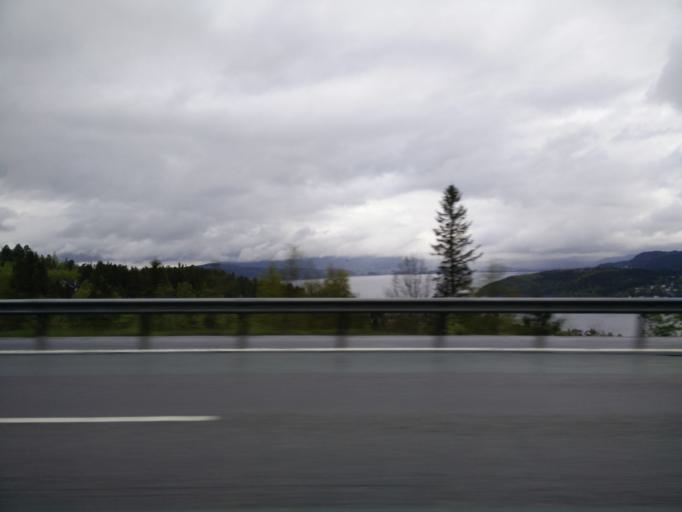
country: NO
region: Sor-Trondelag
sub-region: Malvik
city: Hommelvik
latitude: 63.4180
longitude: 10.7643
